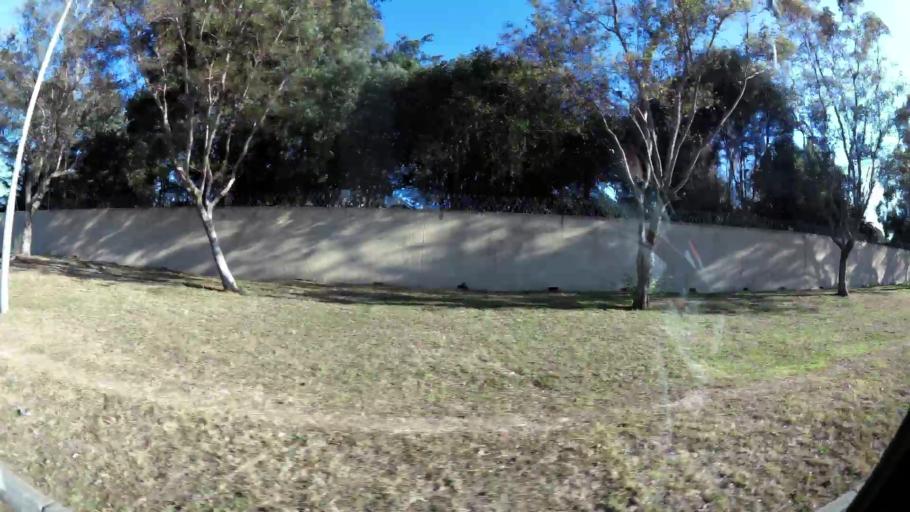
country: ZA
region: Gauteng
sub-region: City of Johannesburg Metropolitan Municipality
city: Midrand
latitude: -26.0292
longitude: 28.0485
